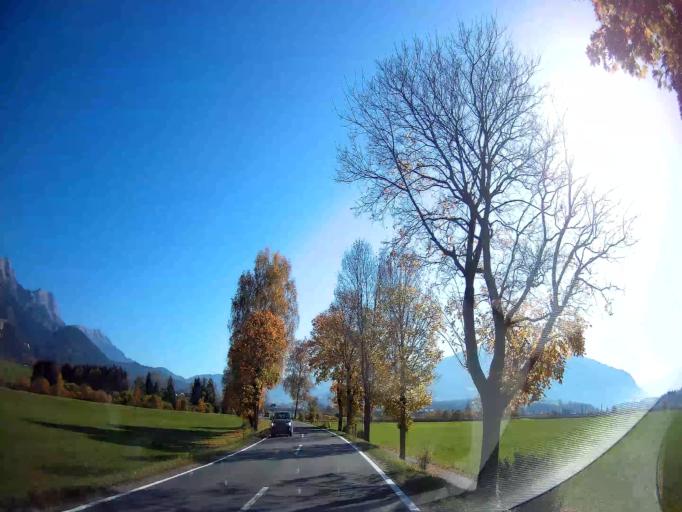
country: AT
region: Salzburg
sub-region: Politischer Bezirk Zell am See
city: Saalfelden am Steinernen Meer
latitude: 47.4378
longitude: 12.8210
